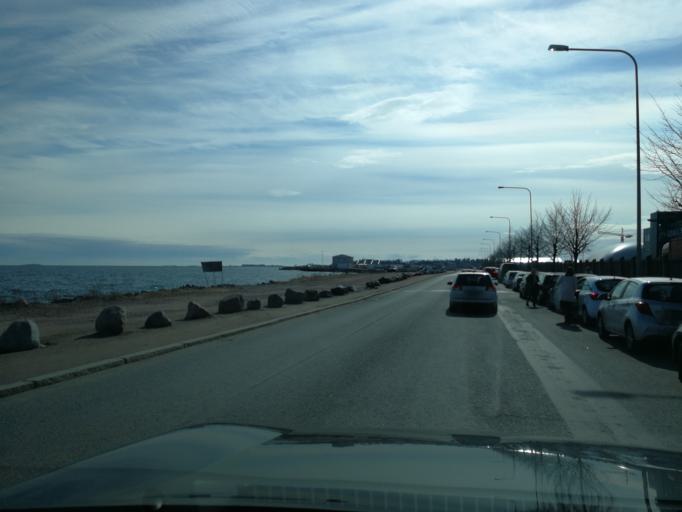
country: FI
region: Uusimaa
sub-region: Helsinki
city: Helsinki
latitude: 60.1514
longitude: 24.9293
